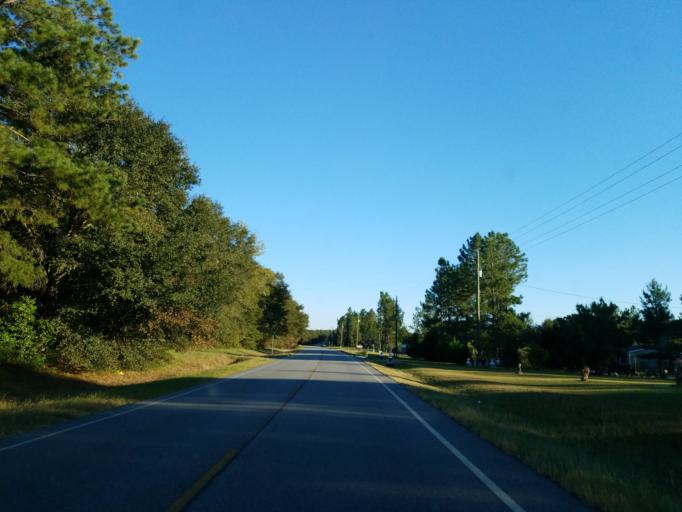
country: US
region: Georgia
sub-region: Worth County
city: Sylvester
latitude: 31.5849
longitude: -83.8604
